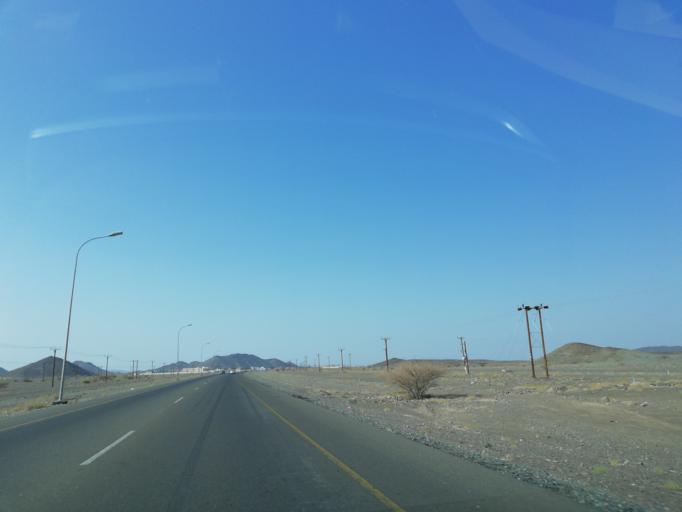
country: OM
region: Ash Sharqiyah
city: Ibra'
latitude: 22.7349
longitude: 58.1505
